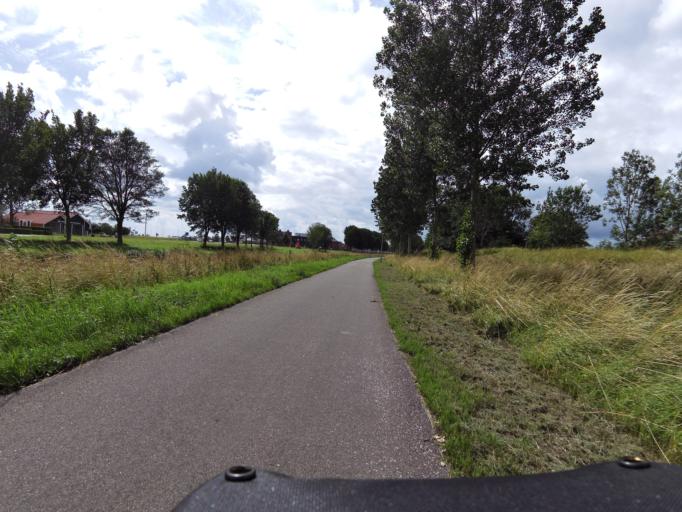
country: NL
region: South Holland
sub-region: Gemeente Goeree-Overflakkee
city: Goedereede
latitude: 51.8180
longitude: 3.9854
